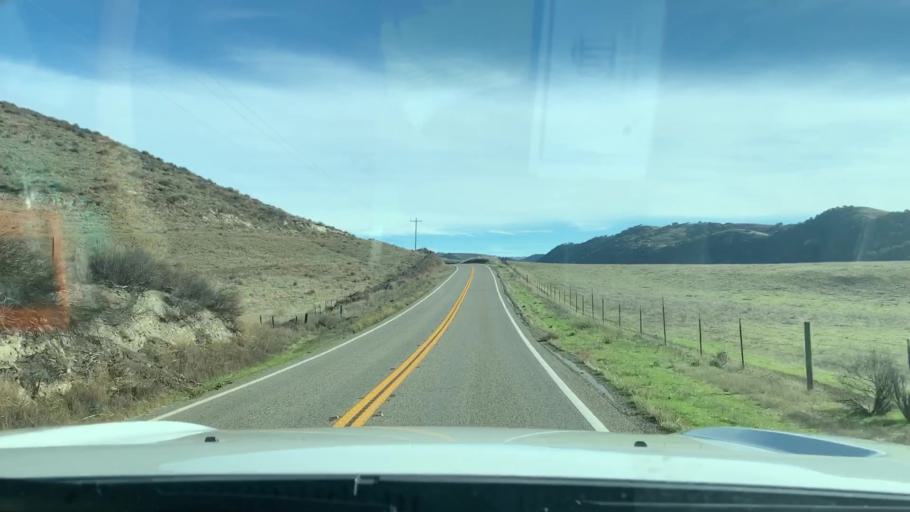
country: US
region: California
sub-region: Monterey County
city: King City
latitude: 36.1654
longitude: -120.8596
